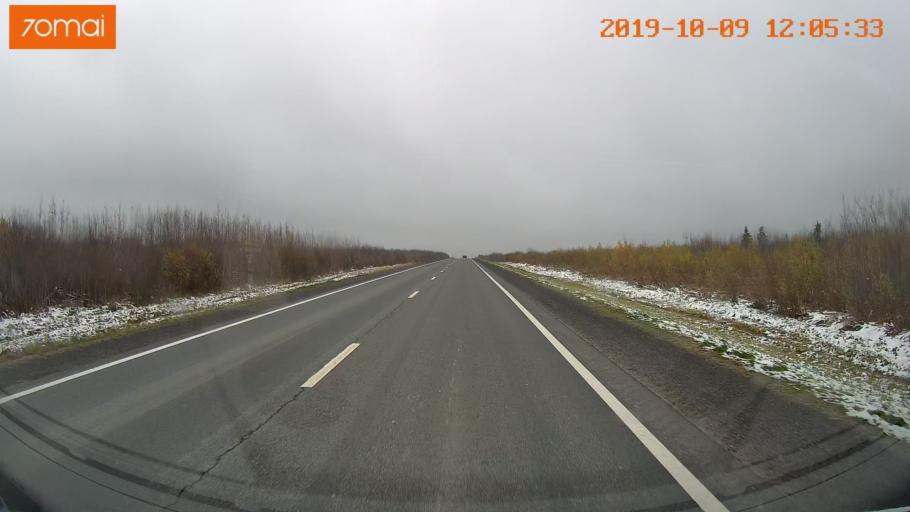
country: RU
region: Jaroslavl
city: Prechistoye
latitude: 58.6257
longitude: 40.3300
